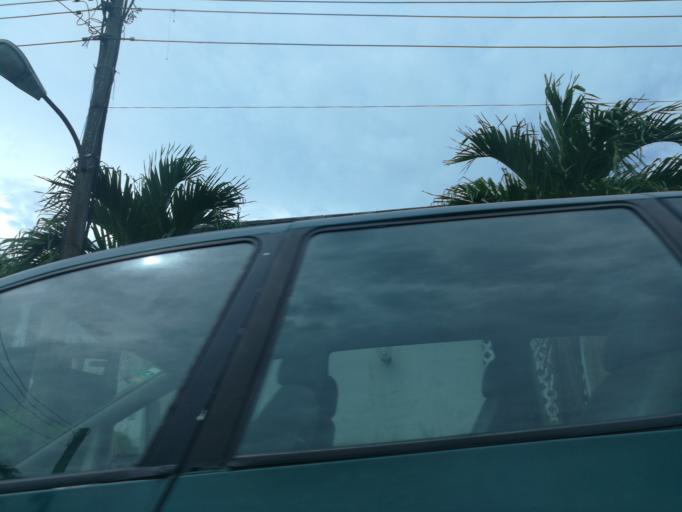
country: NG
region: Lagos
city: Ikoyi
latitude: 6.4409
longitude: 3.4766
